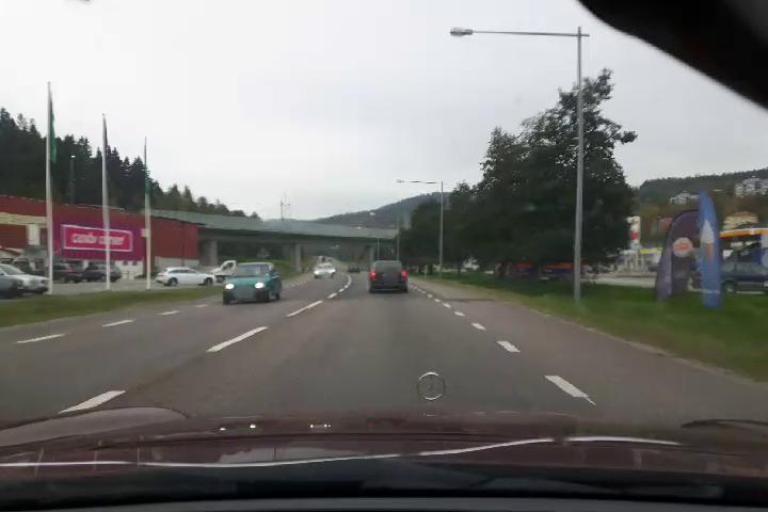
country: SE
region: Vaesternorrland
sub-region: OErnskoeldsviks Kommun
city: Ornskoldsvik
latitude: 63.2925
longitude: 18.7008
